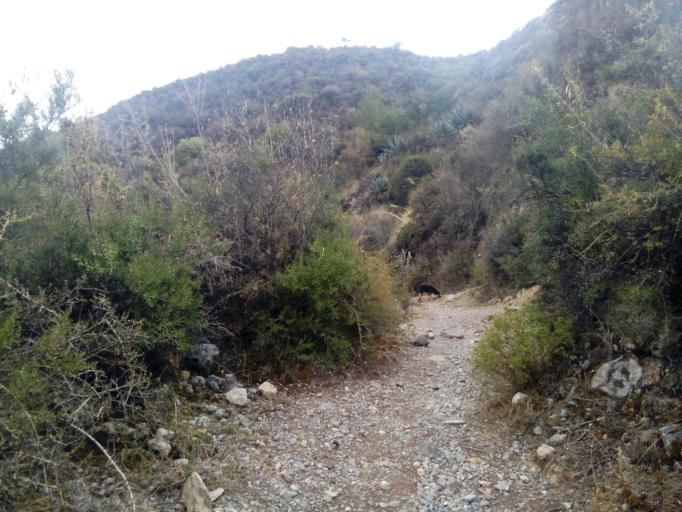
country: PE
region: Ayacucho
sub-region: Provincia de Victor Fajardo
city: Canaria
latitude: -13.9009
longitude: -73.9324
